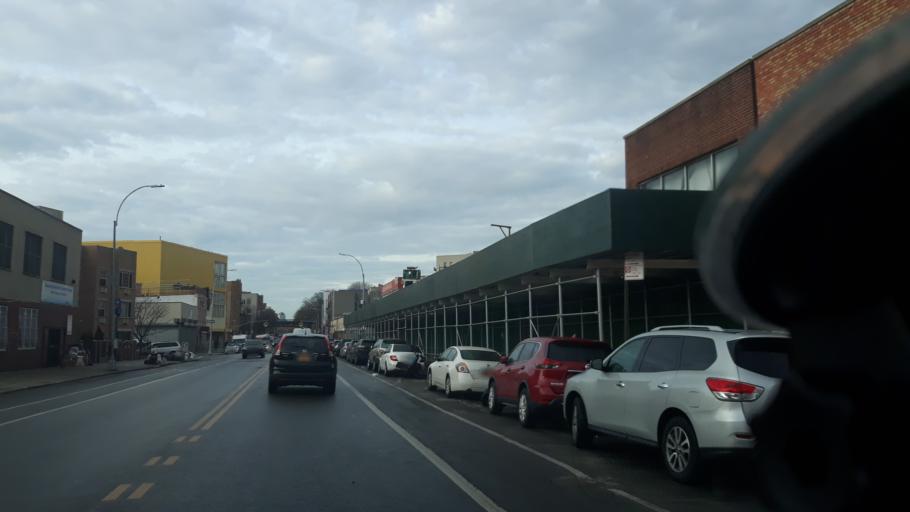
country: US
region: New York
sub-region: Kings County
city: Brooklyn
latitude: 40.6679
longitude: -73.9210
